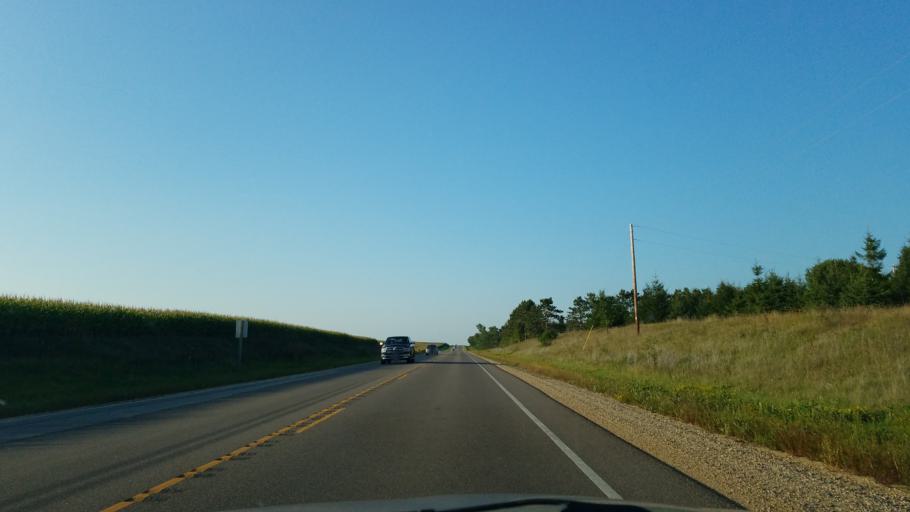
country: US
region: Wisconsin
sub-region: Saint Croix County
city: Baldwin
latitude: 45.0797
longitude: -92.3753
